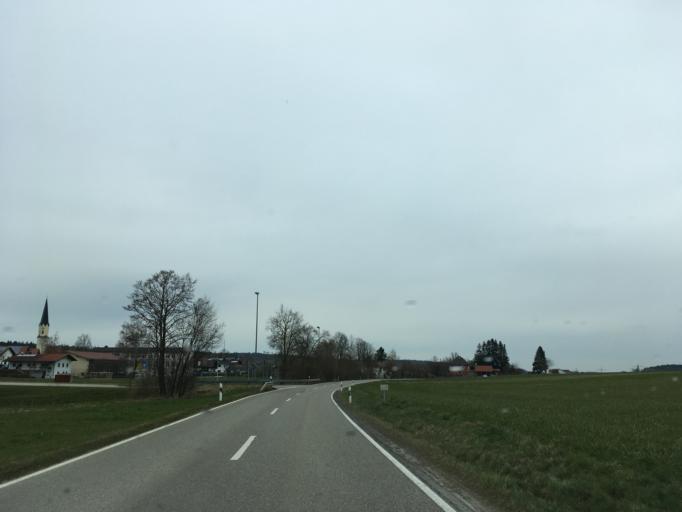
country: DE
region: Bavaria
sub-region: Upper Bavaria
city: Schnaitsee
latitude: 48.1019
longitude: 12.4087
